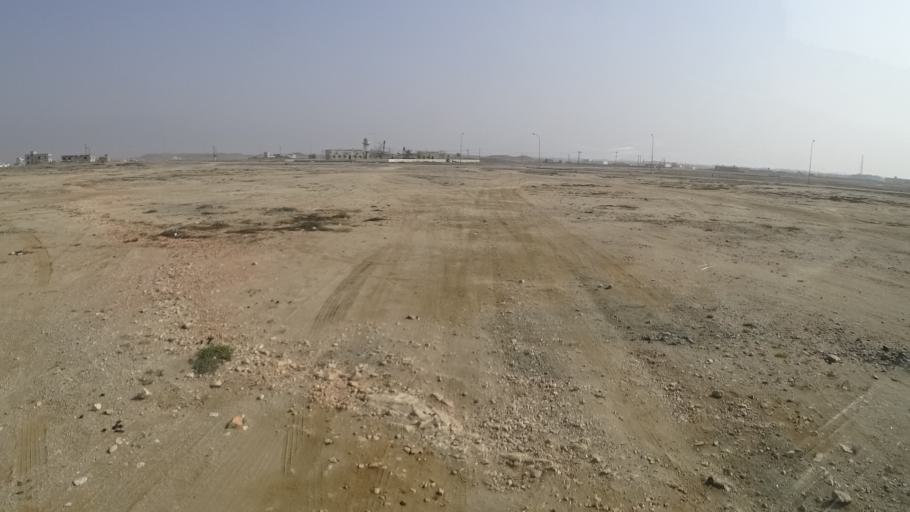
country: OM
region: Zufar
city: Salalah
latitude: 16.9625
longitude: 54.7378
